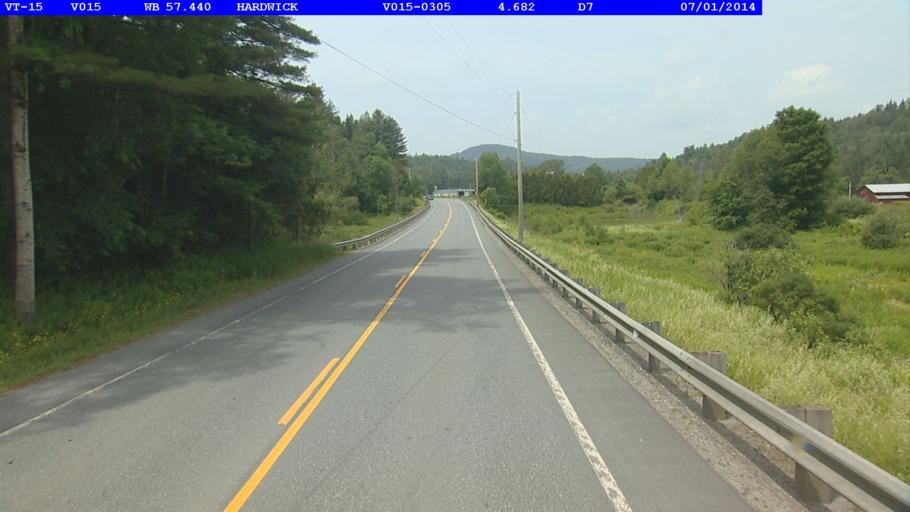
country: US
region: Vermont
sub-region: Caledonia County
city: Hardwick
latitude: 44.5026
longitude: -72.3434
